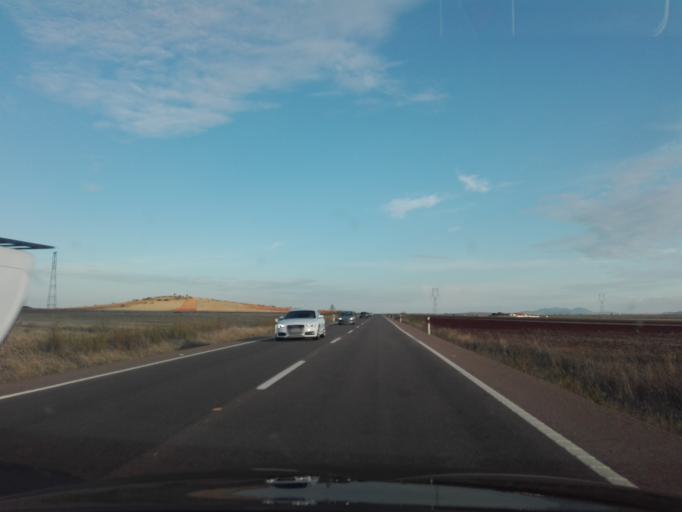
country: ES
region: Extremadura
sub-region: Provincia de Badajoz
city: Usagre
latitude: 38.3601
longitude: -6.2182
